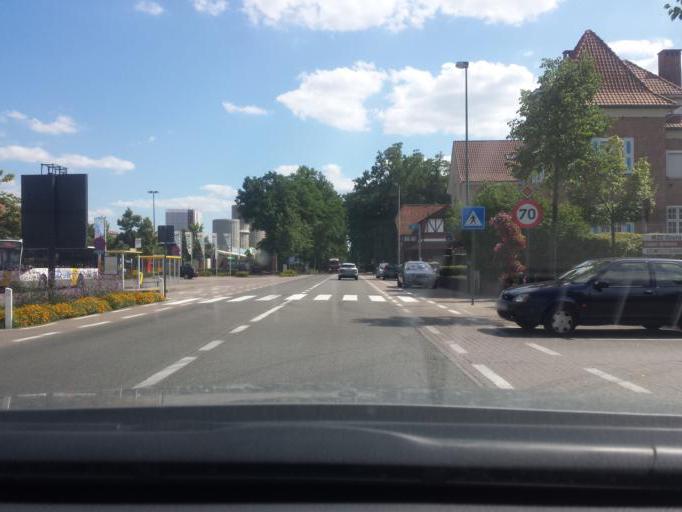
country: BE
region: Flanders
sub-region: Provincie Limburg
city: Beringen
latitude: 51.0713
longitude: 5.2206
